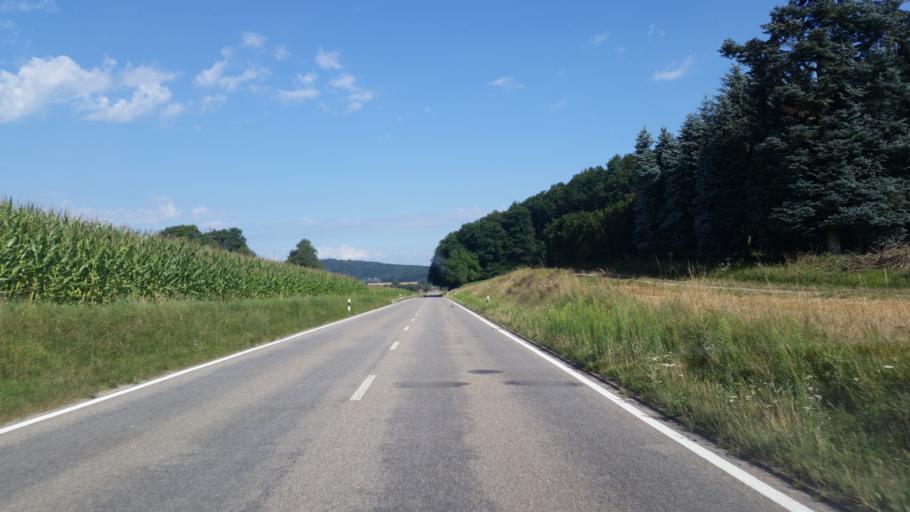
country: CH
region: Zurich
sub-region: Bezirk Dielsdorf
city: Neerach
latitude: 47.5290
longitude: 8.4893
